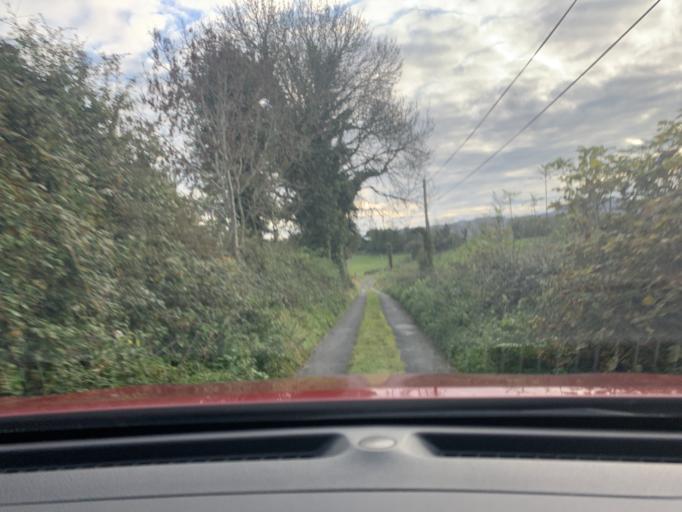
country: IE
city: Ballisodare
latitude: 54.2347
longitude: -8.4988
